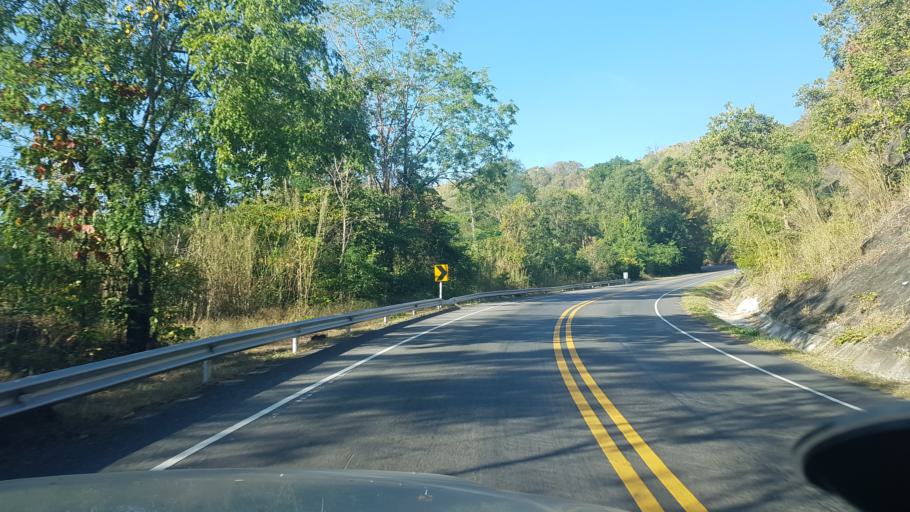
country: TH
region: Phetchabun
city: Lom Sak
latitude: 16.7427
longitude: 101.3930
